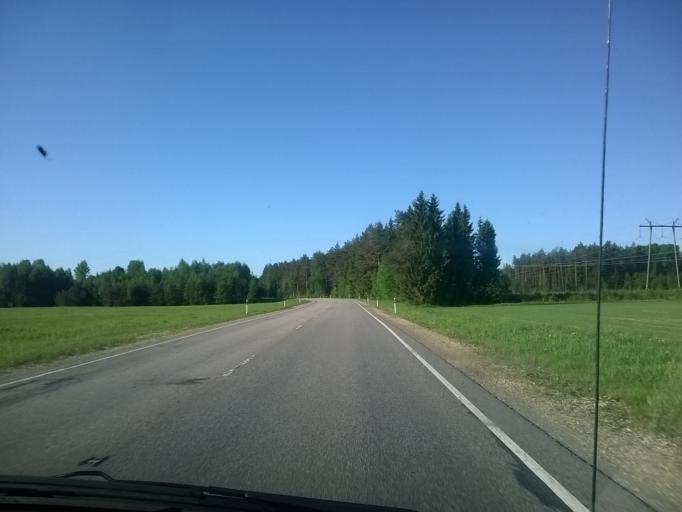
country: EE
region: Valgamaa
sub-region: Valga linn
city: Valga
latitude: 57.8955
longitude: 26.1663
